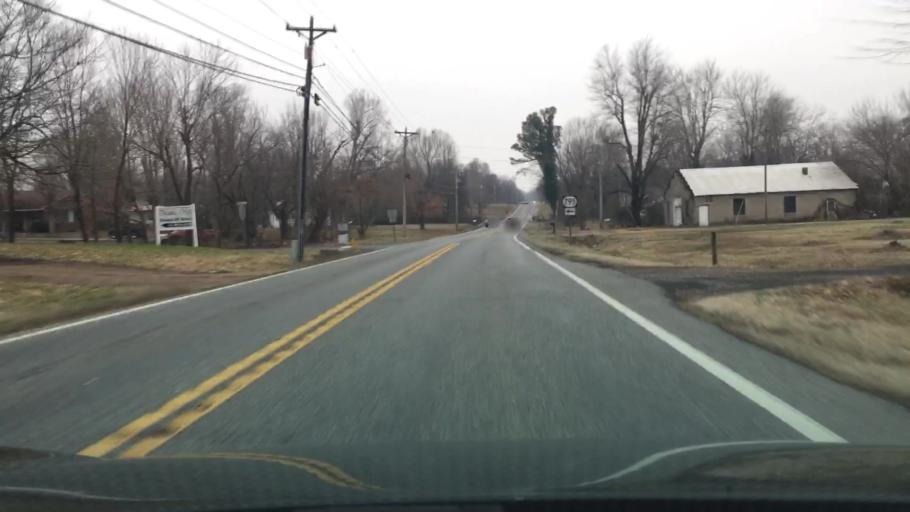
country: US
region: Kentucky
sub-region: Livingston County
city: Ledbetter
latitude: 36.9694
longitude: -88.4596
